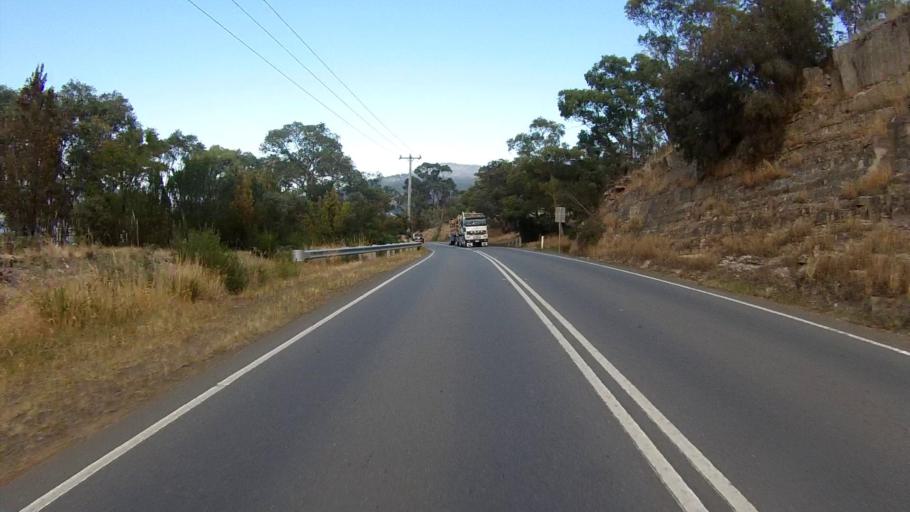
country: AU
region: Tasmania
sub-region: Brighton
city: Bridgewater
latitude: -42.7253
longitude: 147.1968
